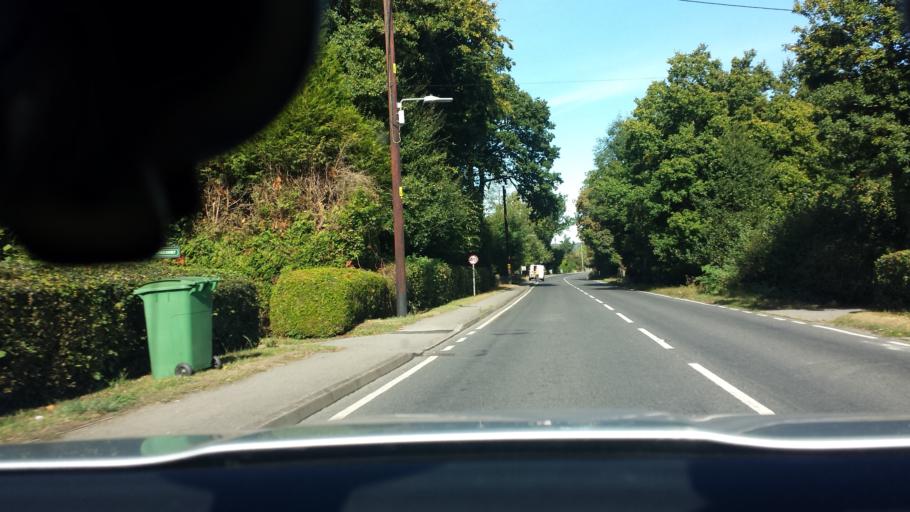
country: GB
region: England
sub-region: Kent
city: Staplehurst
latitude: 51.1761
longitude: 0.5523
